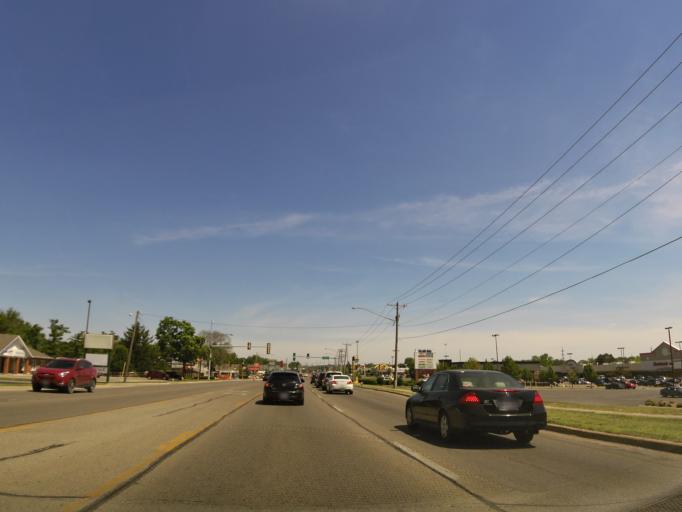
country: US
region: Illinois
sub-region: Vermilion County
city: Danville
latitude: 40.1718
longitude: -87.6307
